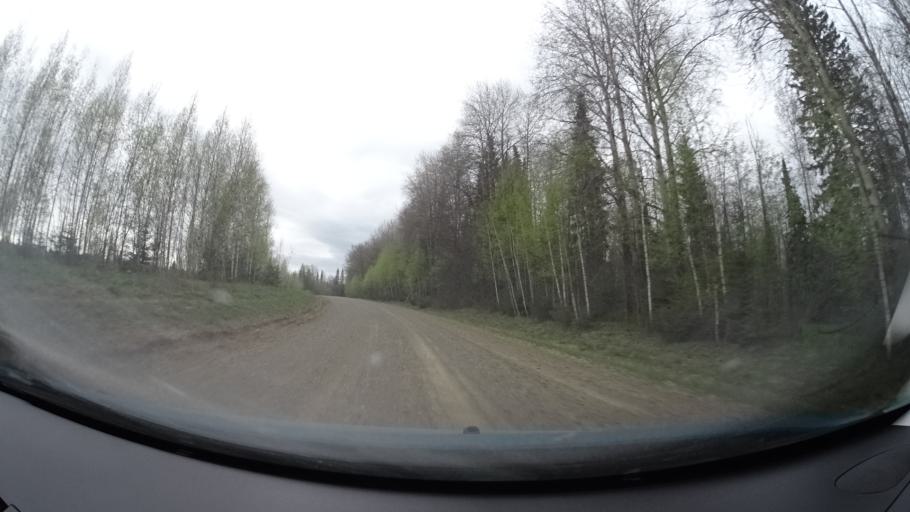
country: RU
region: Perm
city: Kuyeda
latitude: 56.6011
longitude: 55.7119
